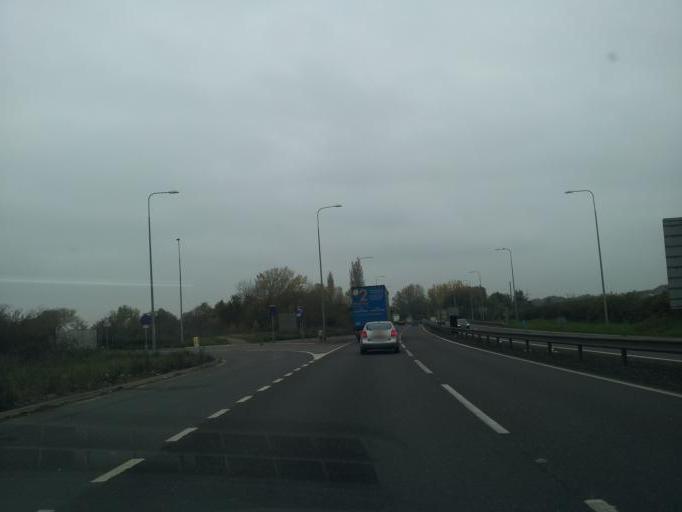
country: GB
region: England
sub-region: Bedford
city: Roxton
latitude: 52.1866
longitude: -0.3035
